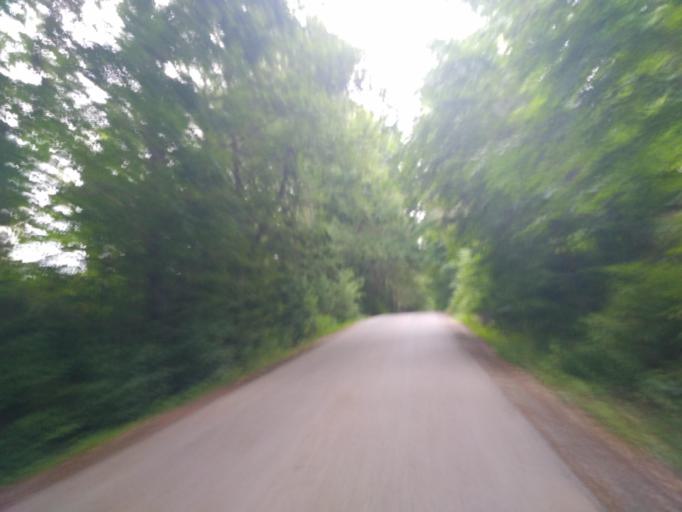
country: PL
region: Subcarpathian Voivodeship
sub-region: Powiat ropczycko-sedziszowski
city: Niedzwiada
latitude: 50.0281
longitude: 21.5284
